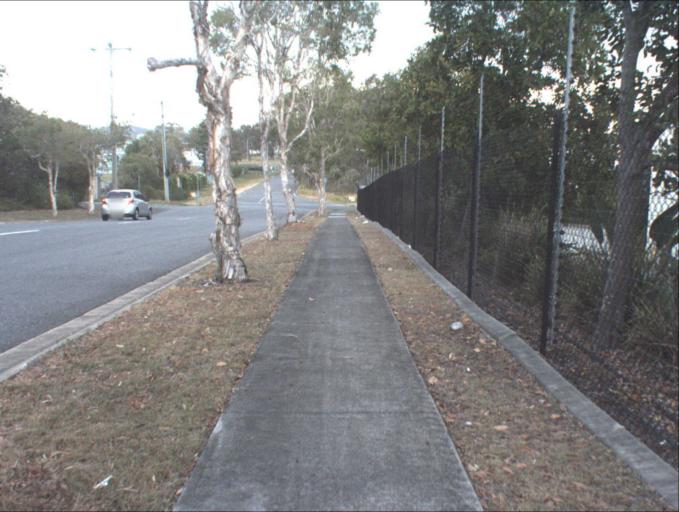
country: AU
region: Queensland
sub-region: Logan
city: Beenleigh
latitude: -27.6834
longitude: 153.1939
